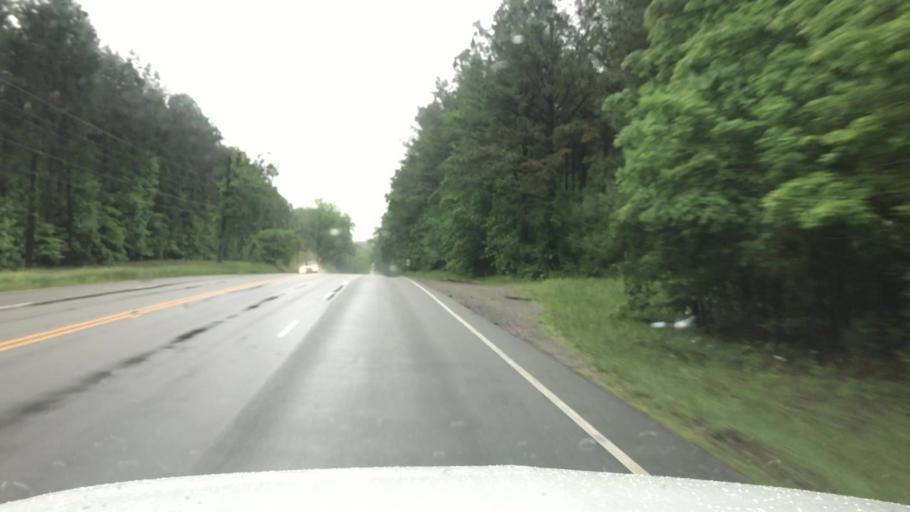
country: US
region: Virginia
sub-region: Hanover County
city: Ashland
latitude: 37.8248
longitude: -77.4716
